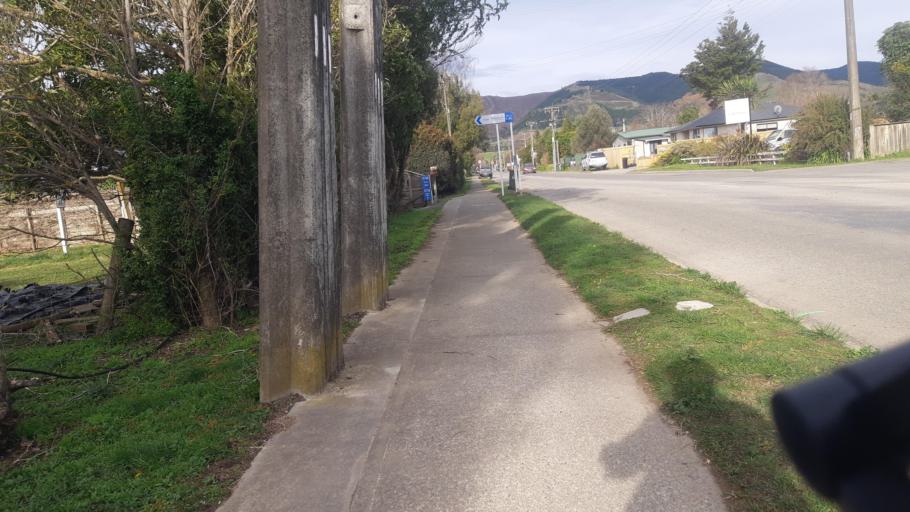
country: NZ
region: Tasman
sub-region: Tasman District
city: Richmond
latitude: -41.3526
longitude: 173.1520
